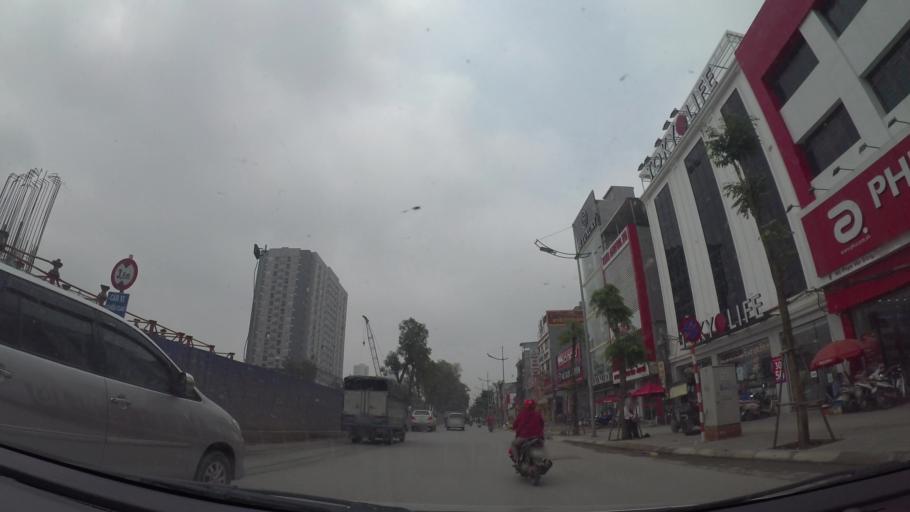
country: VN
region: Ha Noi
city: Cau Dien
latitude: 21.0453
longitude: 105.7810
